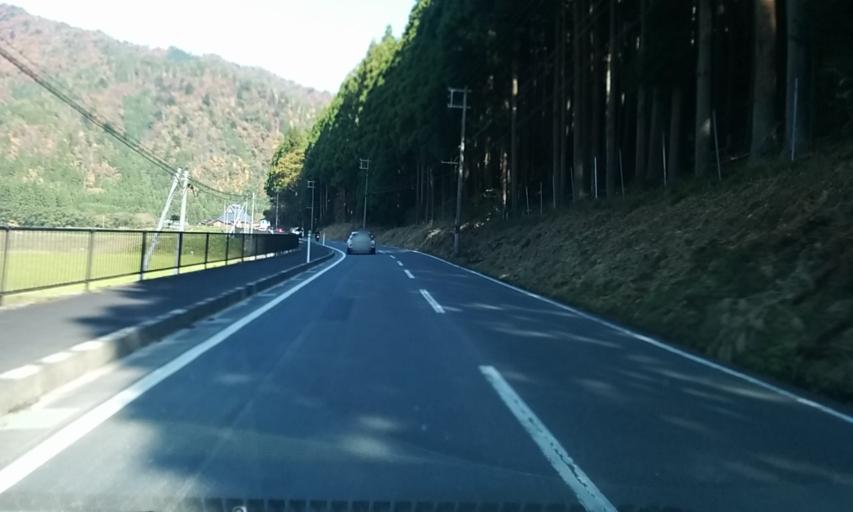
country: JP
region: Fukui
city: Obama
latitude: 35.2945
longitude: 135.6018
